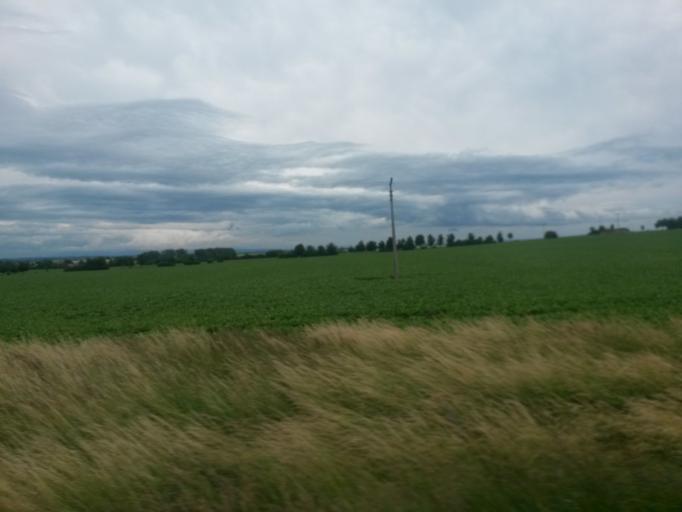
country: CZ
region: Olomoucky
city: Hnevotin
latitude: 49.5595
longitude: 17.1954
